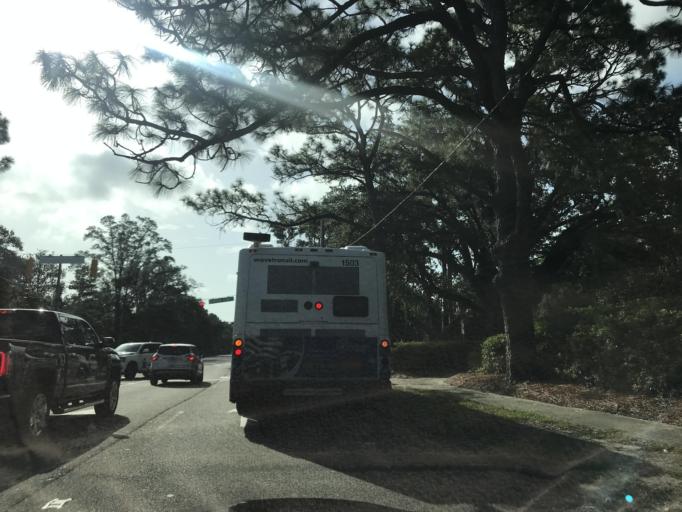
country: US
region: North Carolina
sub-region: New Hanover County
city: Wilmington
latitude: 34.2214
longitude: -77.9160
